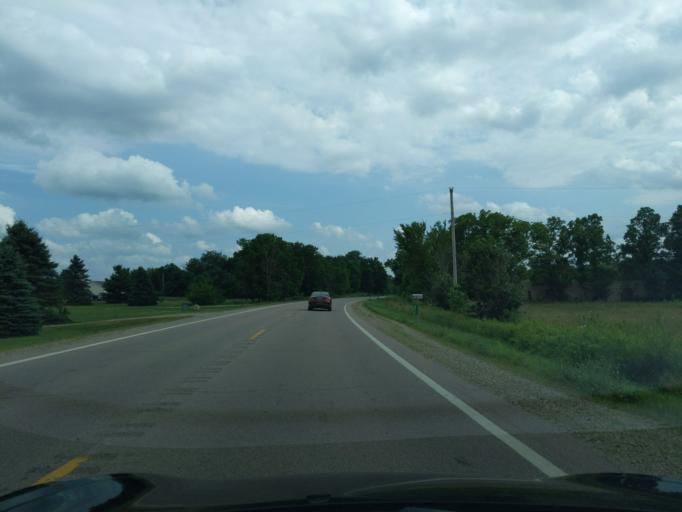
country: US
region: Michigan
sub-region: Eaton County
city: Eaton Rapids
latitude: 42.4482
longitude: -84.6500
